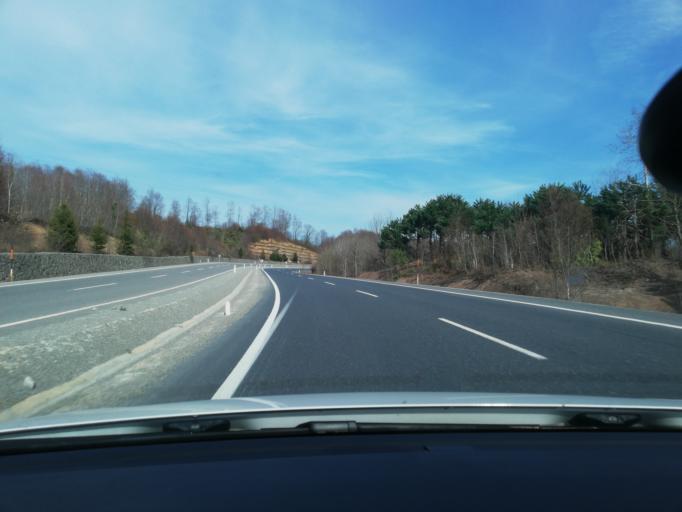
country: TR
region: Zonguldak
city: Ormanli
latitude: 41.3323
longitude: 31.5914
